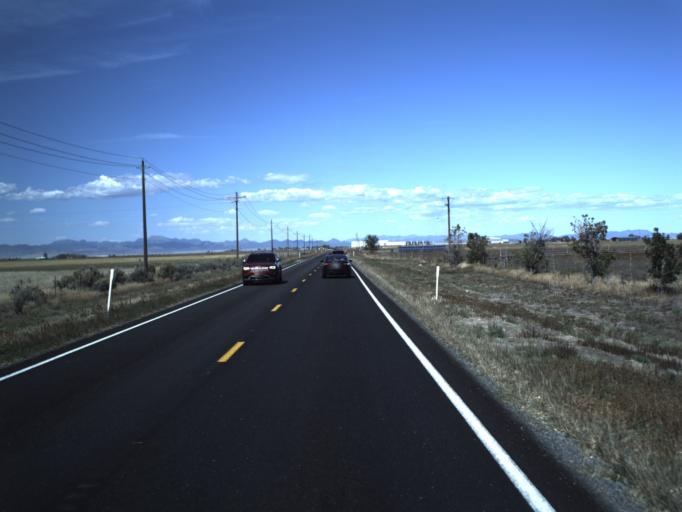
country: US
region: Utah
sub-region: Washington County
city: Enterprise
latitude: 37.6617
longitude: -113.6612
